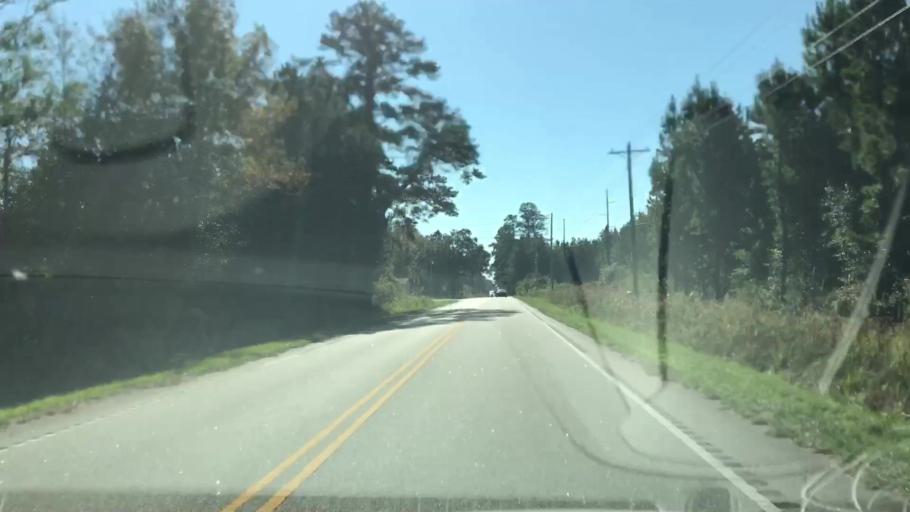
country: US
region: South Carolina
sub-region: Jasper County
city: Ridgeland
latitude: 32.5194
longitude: -80.8905
